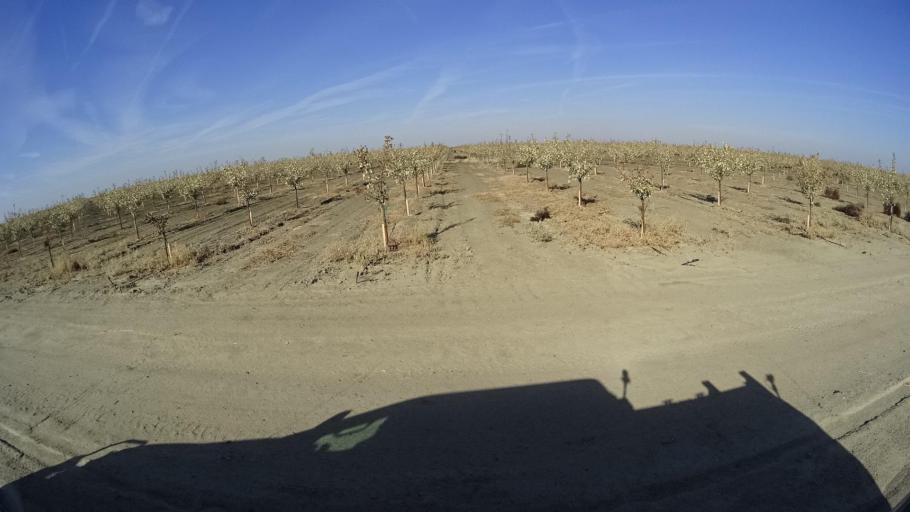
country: US
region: California
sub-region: Kern County
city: Wasco
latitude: 35.7032
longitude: -119.4127
